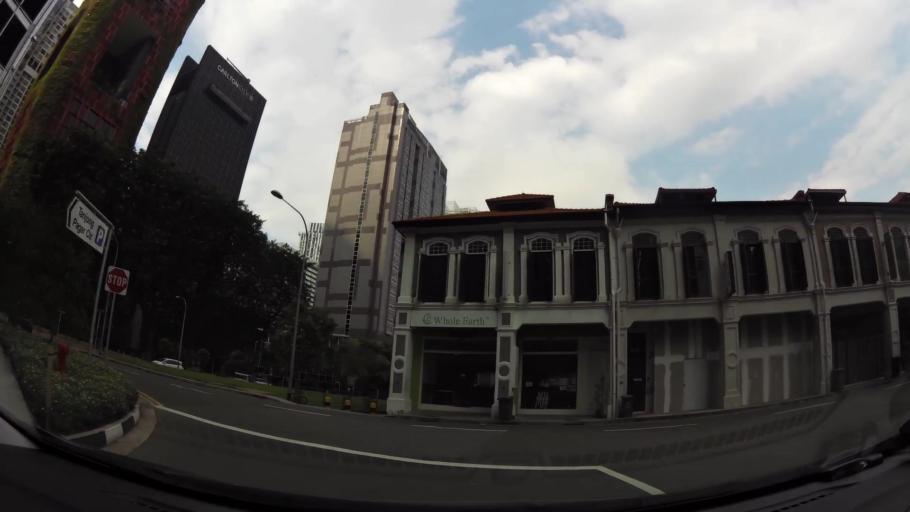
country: SG
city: Singapore
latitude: 1.2771
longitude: 103.8450
